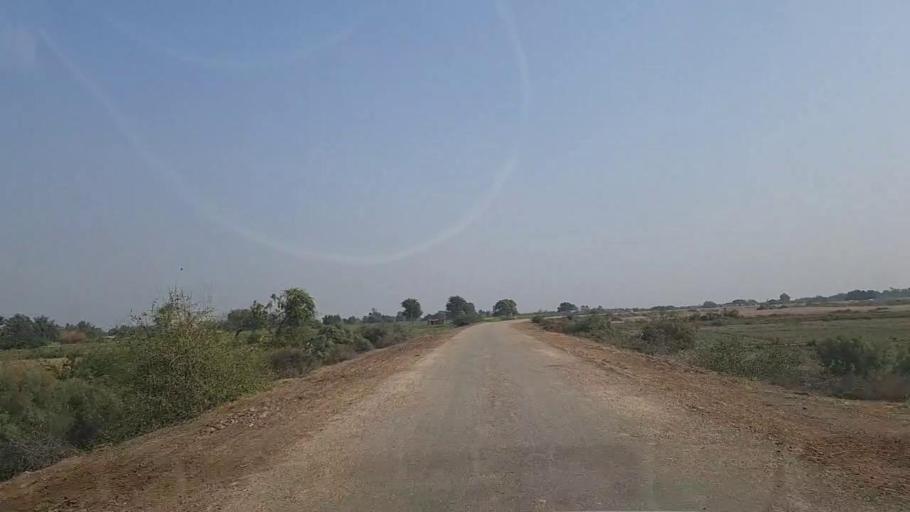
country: PK
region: Sindh
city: Keti Bandar
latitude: 24.2467
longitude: 67.6968
